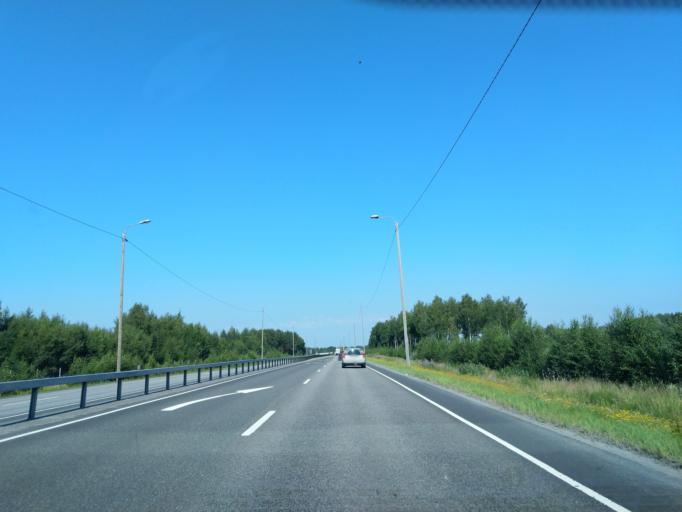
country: FI
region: Satakunta
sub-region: Pori
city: Nakkila
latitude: 61.3431
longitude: 22.0296
